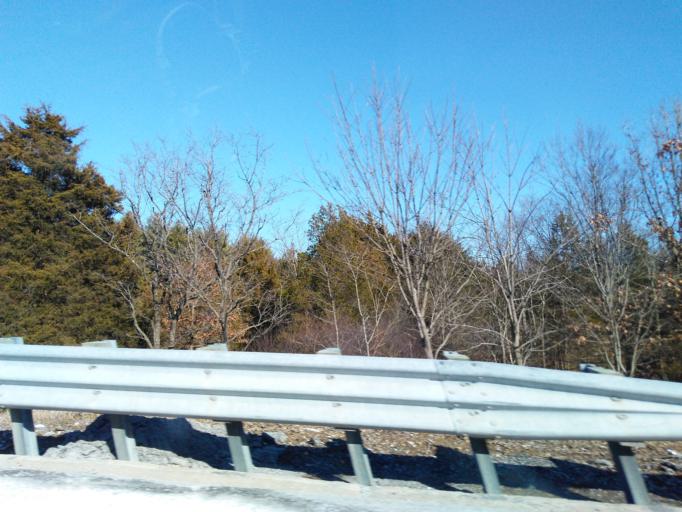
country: US
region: Illinois
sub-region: Johnson County
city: Vienna
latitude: 37.4904
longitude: -88.8934
